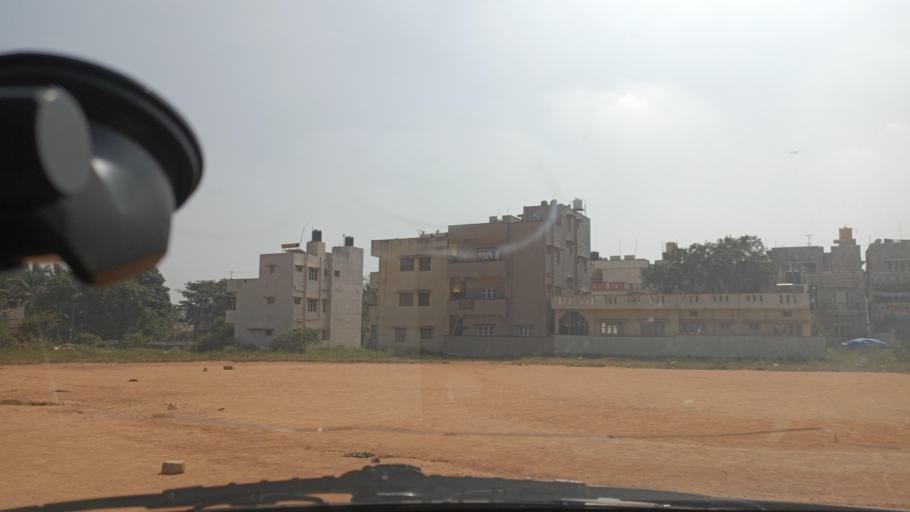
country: IN
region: Karnataka
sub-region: Bangalore Urban
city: Yelahanka
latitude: 13.1123
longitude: 77.6099
